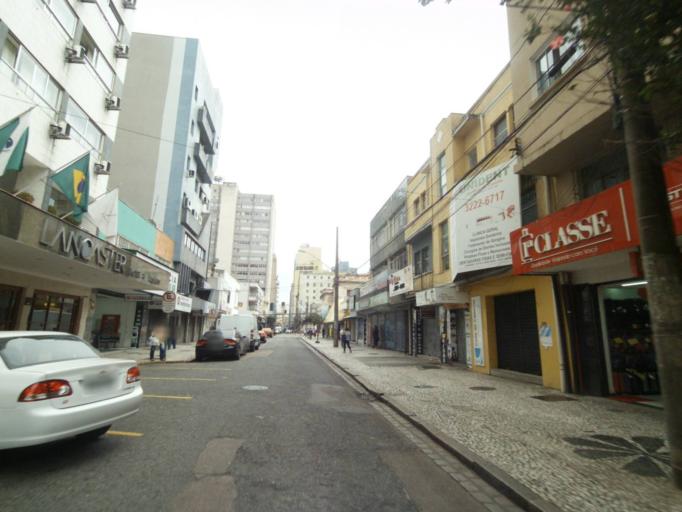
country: BR
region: Parana
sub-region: Curitiba
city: Curitiba
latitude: -25.4342
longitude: -49.2732
